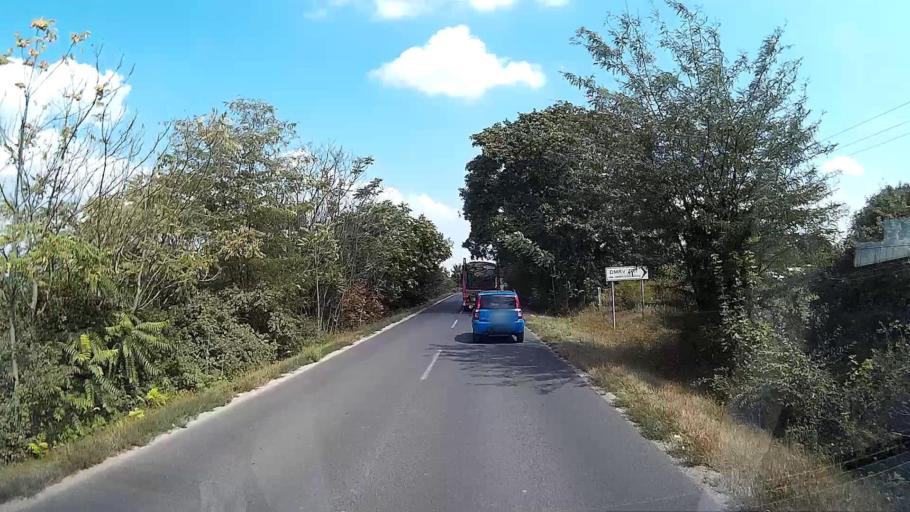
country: HU
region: Pest
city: Budakalasz
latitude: 47.6380
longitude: 19.0642
